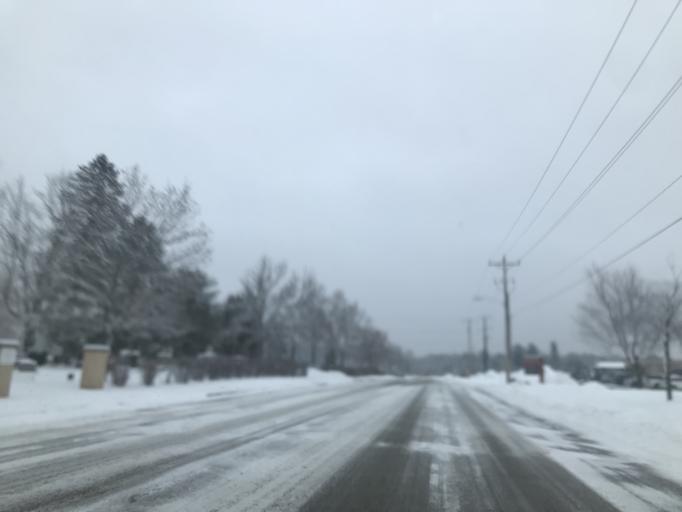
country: US
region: Wisconsin
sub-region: Oconto County
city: Oconto Falls
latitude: 44.8668
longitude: -88.1286
